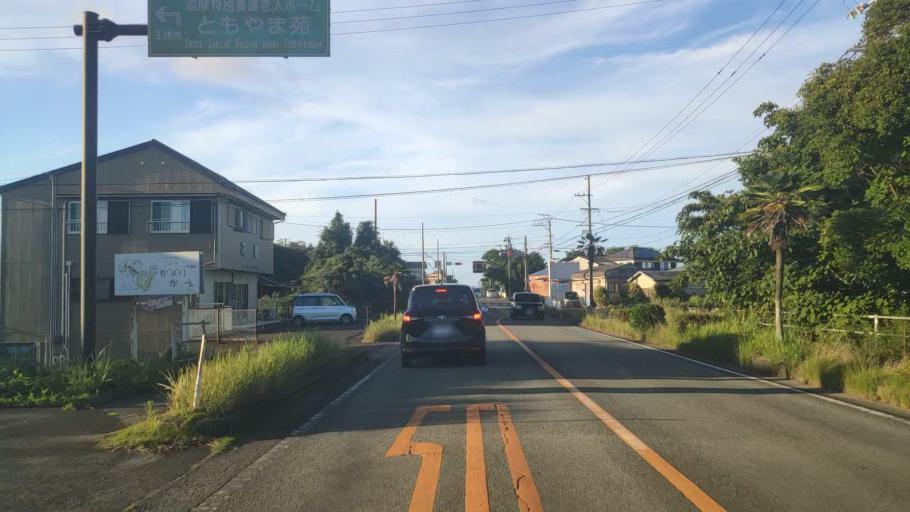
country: JP
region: Mie
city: Toba
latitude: 34.2808
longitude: 136.8807
